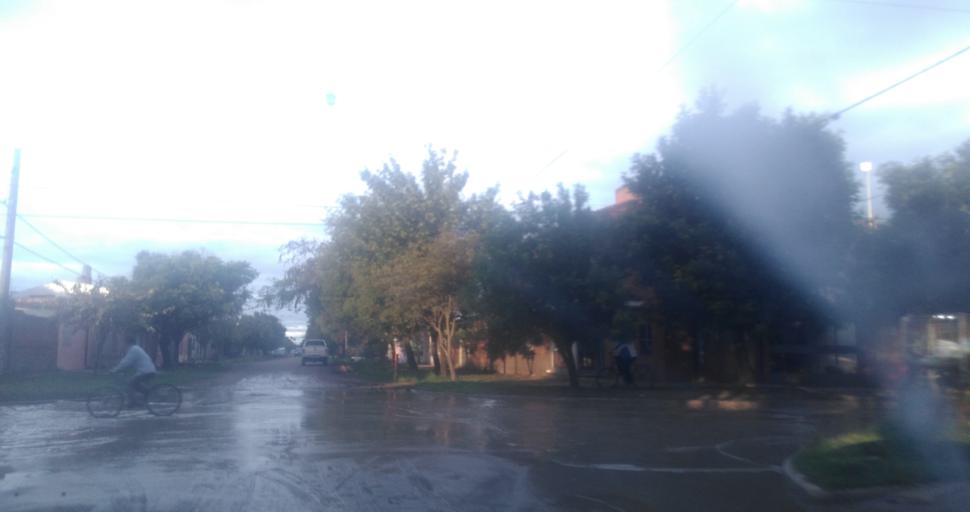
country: AR
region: Chaco
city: Resistencia
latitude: -27.4689
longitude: -58.9737
